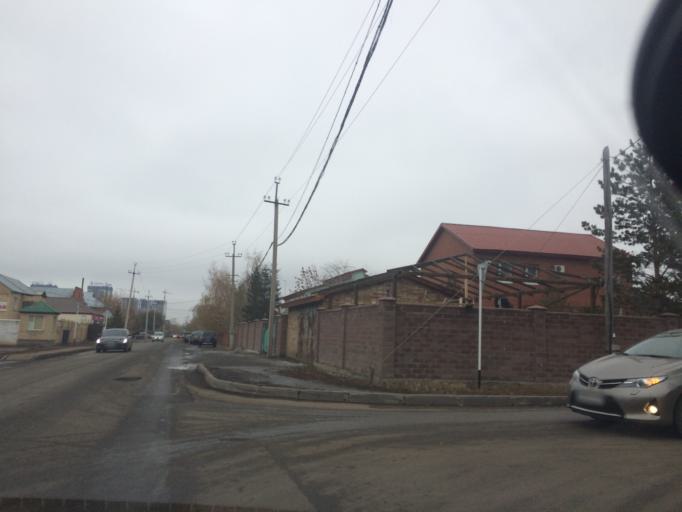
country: KZ
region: Astana Qalasy
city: Astana
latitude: 51.1372
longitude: 71.4209
